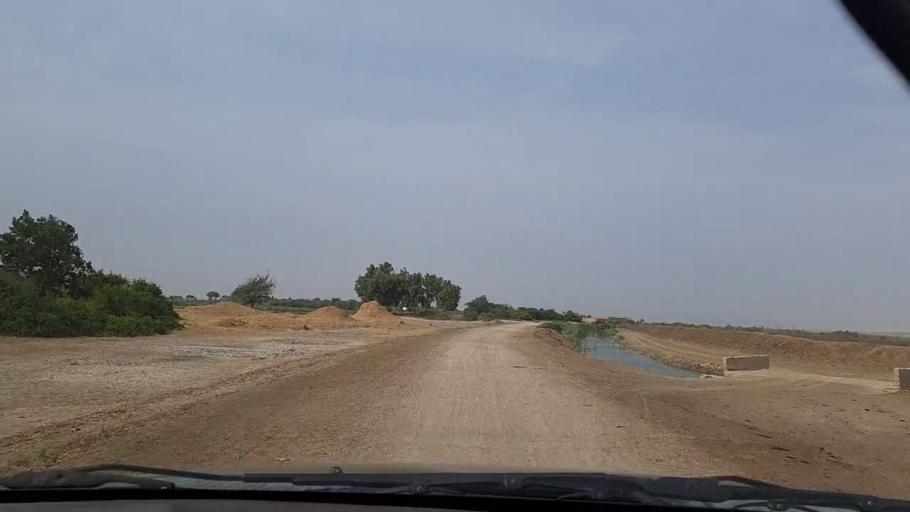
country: PK
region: Sindh
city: Thatta
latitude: 24.5759
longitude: 67.8519
